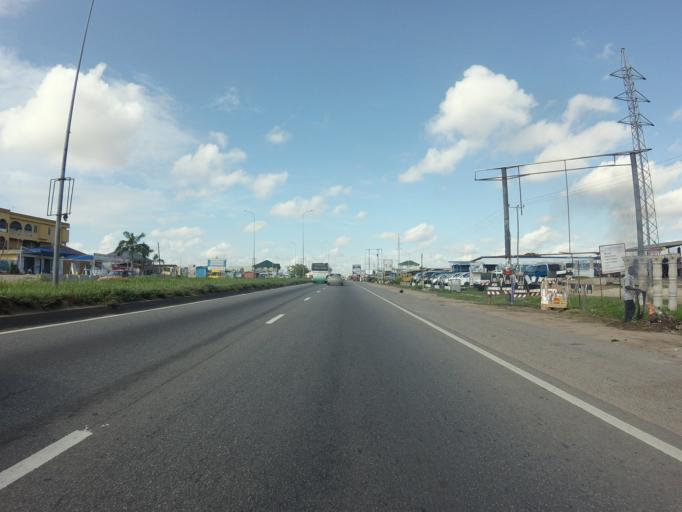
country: GH
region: Central
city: Kasoa
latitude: 5.5417
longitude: -0.3933
